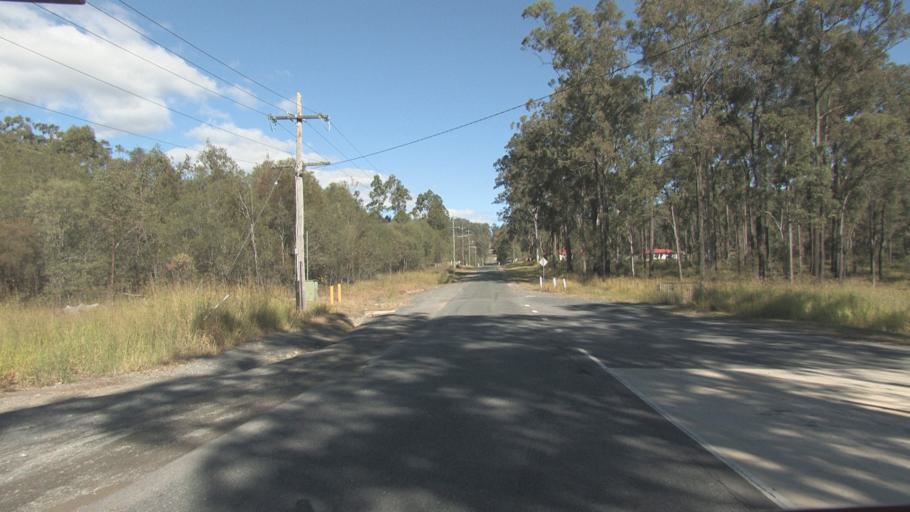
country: AU
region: Queensland
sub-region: Logan
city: Chambers Flat
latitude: -27.8039
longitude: 153.0830
